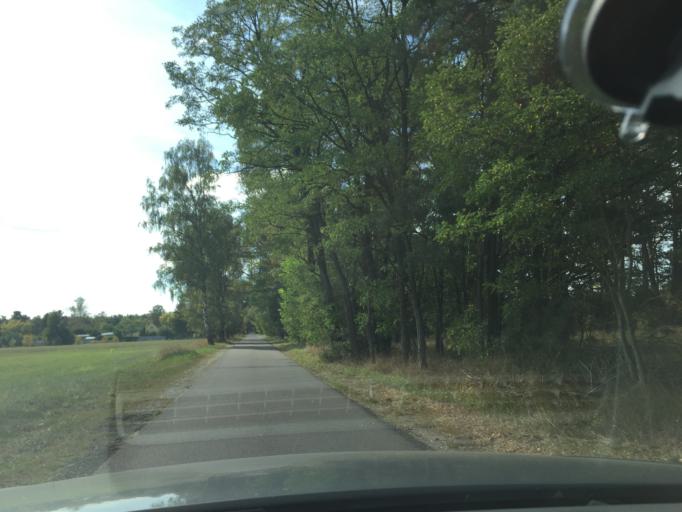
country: DE
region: Brandenburg
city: Spreenhagen
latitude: 52.3649
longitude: 13.8814
